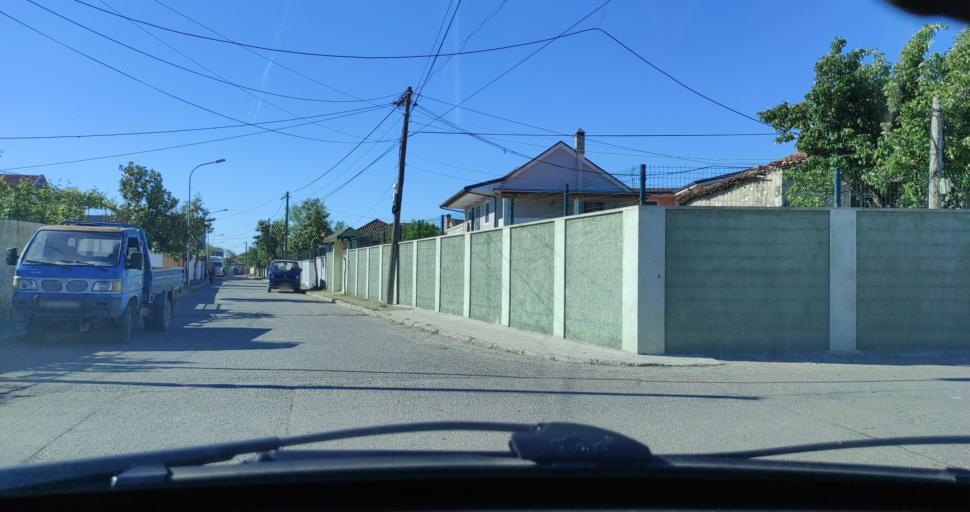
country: AL
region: Shkoder
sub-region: Rrethi i Shkodres
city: Shkoder
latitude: 42.0764
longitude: 19.5005
